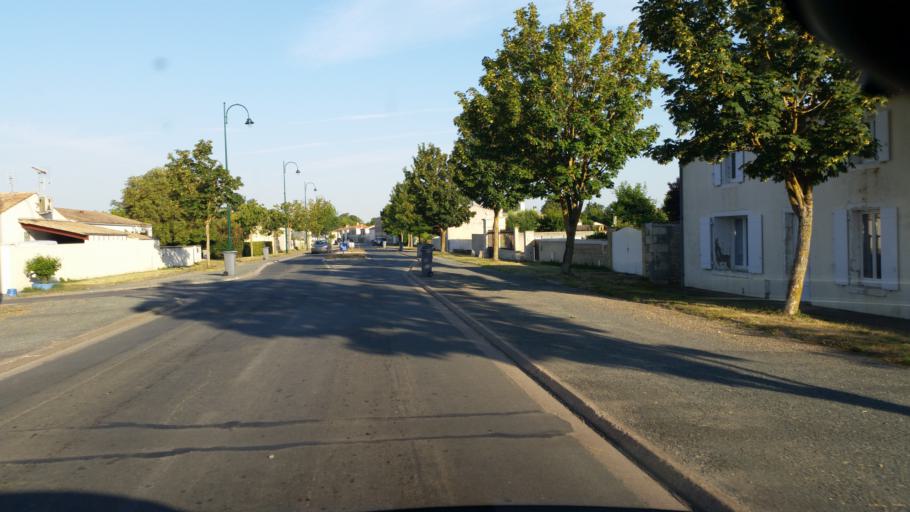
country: FR
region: Poitou-Charentes
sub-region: Departement de la Charente-Maritime
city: Saint-Jean-de-Liversay
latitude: 46.2270
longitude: -0.8565
